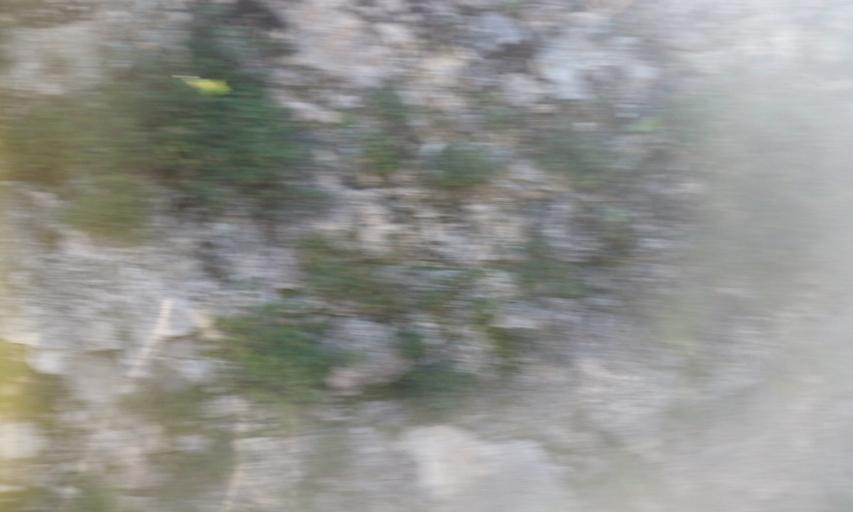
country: PT
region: Guarda
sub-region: Manteigas
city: Manteigas
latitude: 40.4901
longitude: -7.6038
